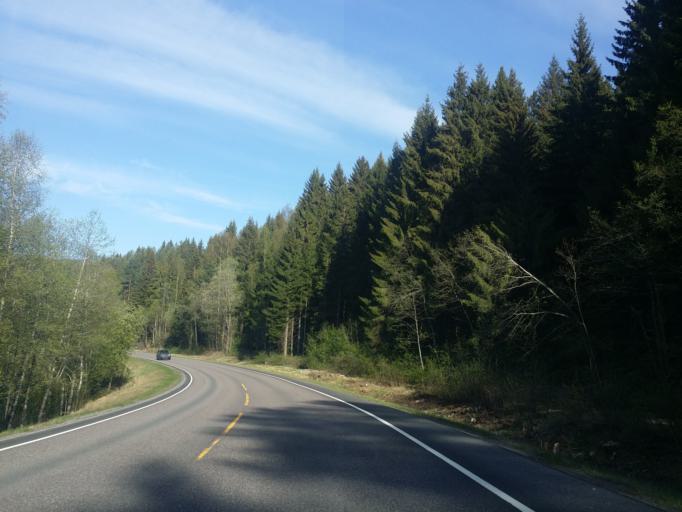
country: NO
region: Telemark
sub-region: Hjartdal
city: Sauland
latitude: 59.6088
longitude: 8.9736
